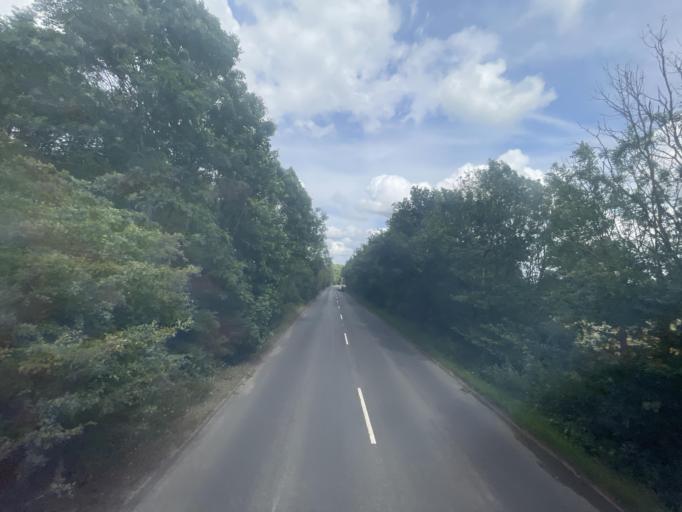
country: GB
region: England
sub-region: Kent
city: Westerham
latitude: 51.2759
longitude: 0.0779
